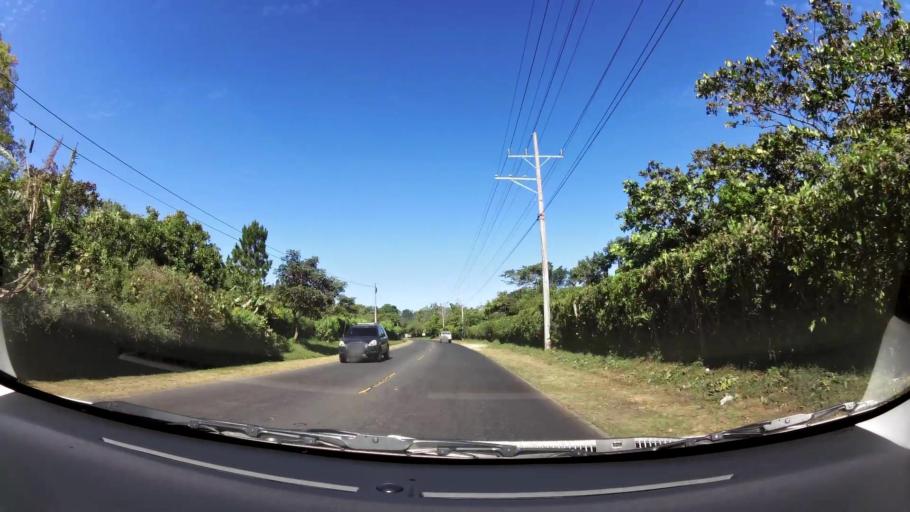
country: SV
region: Ahuachapan
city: Concepcion de Ataco
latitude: 13.8533
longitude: -89.8432
